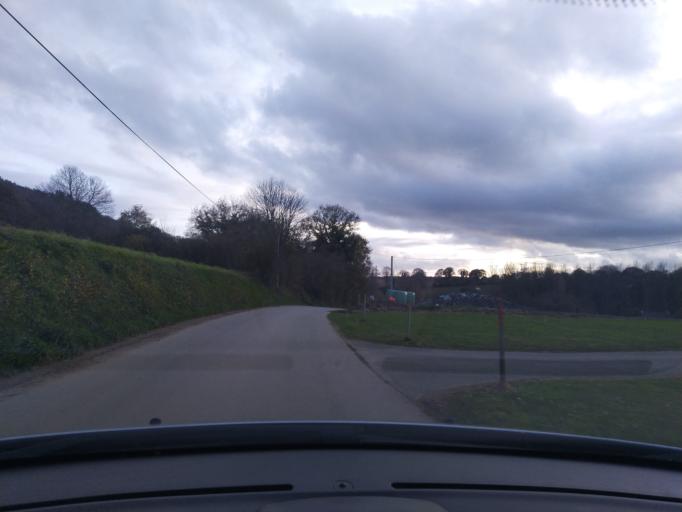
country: FR
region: Brittany
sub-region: Departement du Finistere
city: Guerlesquin
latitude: 48.5586
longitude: -3.6178
